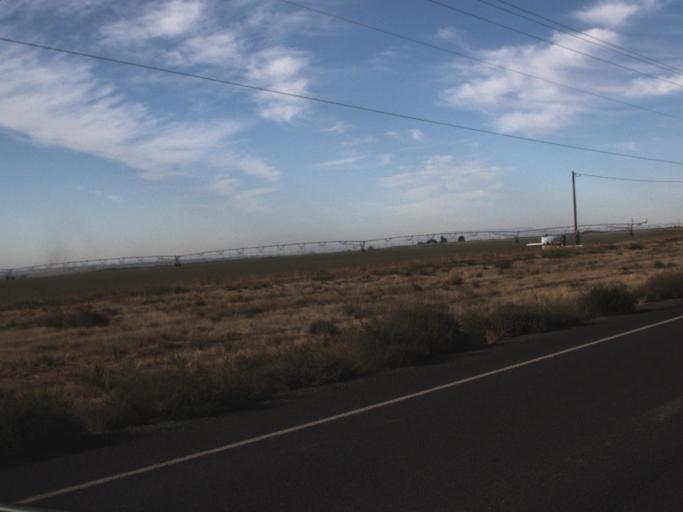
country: US
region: Washington
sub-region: Franklin County
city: Connell
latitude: 46.6636
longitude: -118.9286
